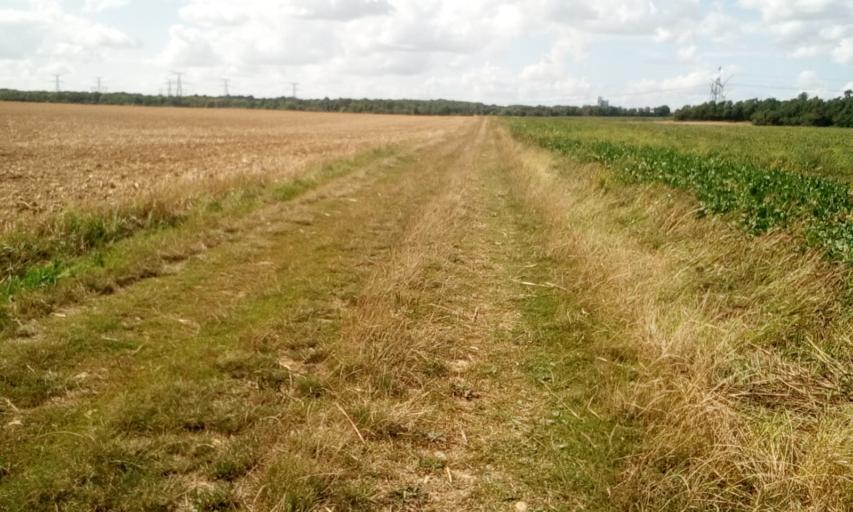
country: FR
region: Lower Normandy
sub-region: Departement du Calvados
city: Bellengreville
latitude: 49.1106
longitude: -0.2347
